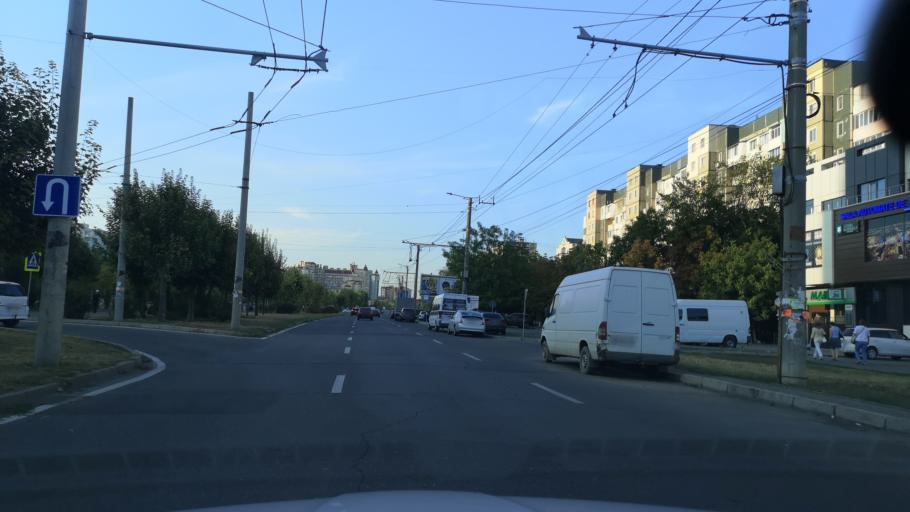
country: MD
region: Chisinau
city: Stauceni
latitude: 47.0478
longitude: 28.8908
